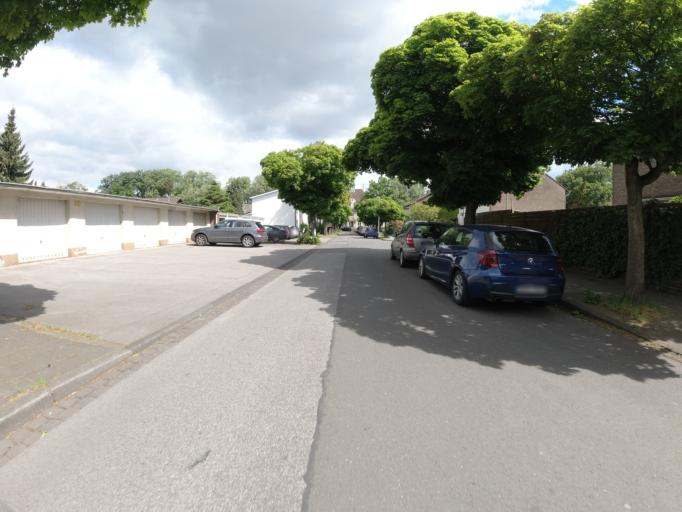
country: DE
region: North Rhine-Westphalia
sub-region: Regierungsbezirk Dusseldorf
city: Hochfeld
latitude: 51.3954
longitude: 6.7002
